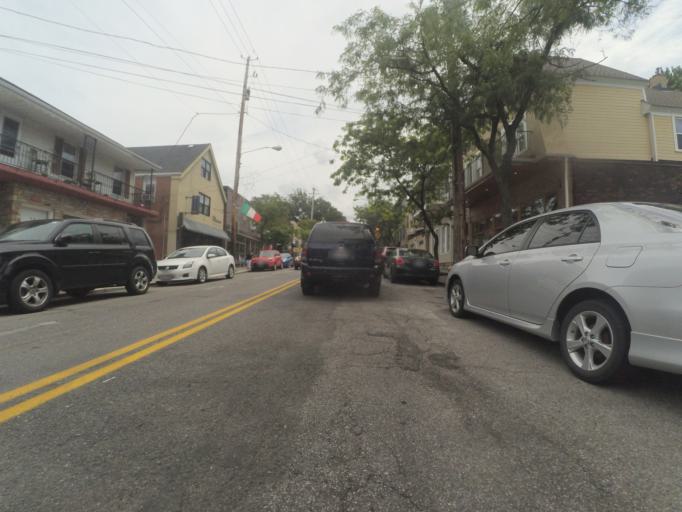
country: US
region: Ohio
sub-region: Cuyahoga County
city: East Cleveland
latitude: 41.5087
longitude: -81.5969
